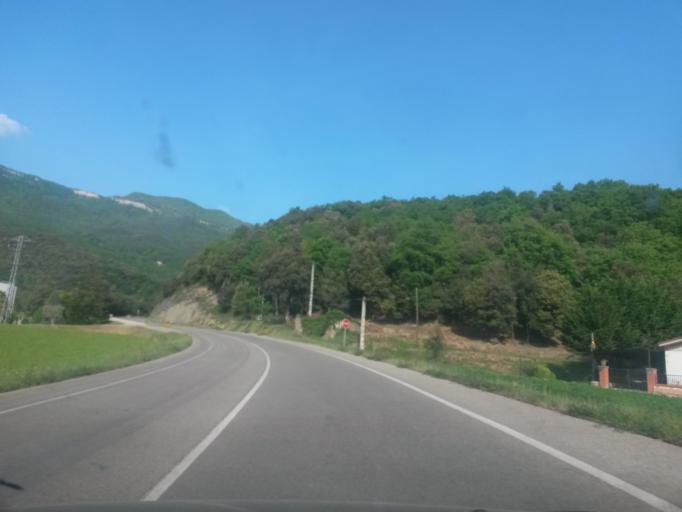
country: ES
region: Catalonia
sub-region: Provincia de Girona
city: les Planes d'Hostoles
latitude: 42.0463
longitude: 2.5573
